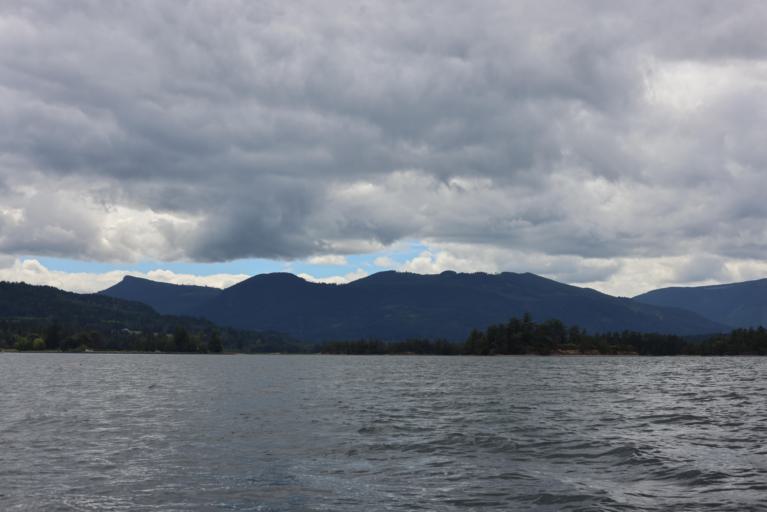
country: CA
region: British Columbia
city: North Cowichan
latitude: 48.8904
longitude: -123.6353
